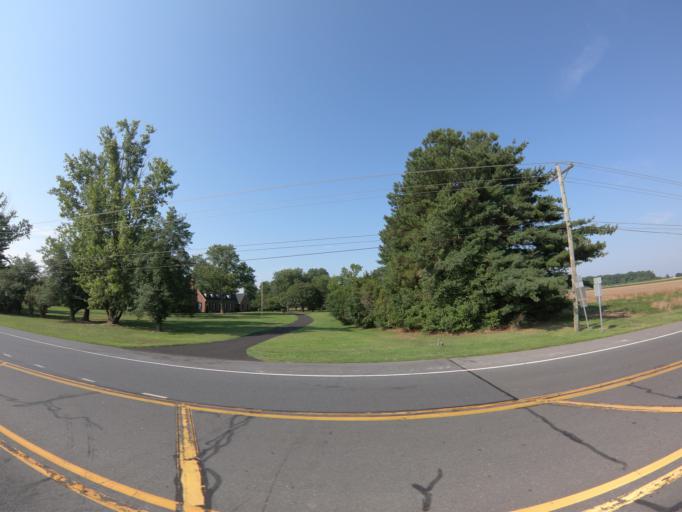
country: US
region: Delaware
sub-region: Sussex County
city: Bridgeville
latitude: 38.7549
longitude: -75.6291
